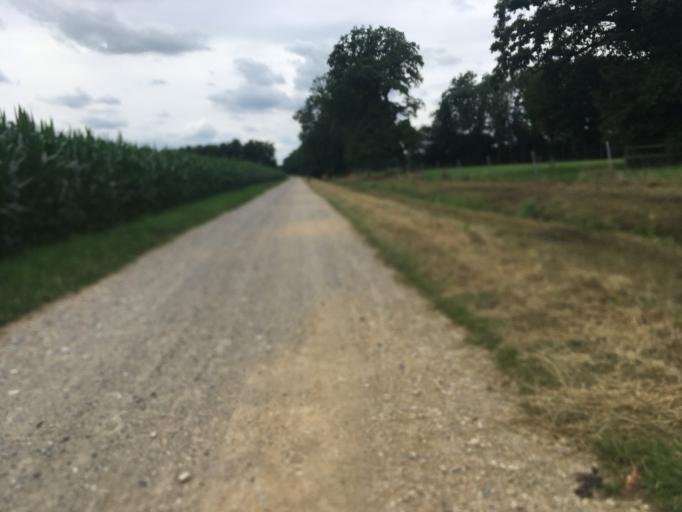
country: CH
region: Vaud
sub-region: Broye-Vully District
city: Avenches
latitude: 46.8946
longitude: 7.0317
